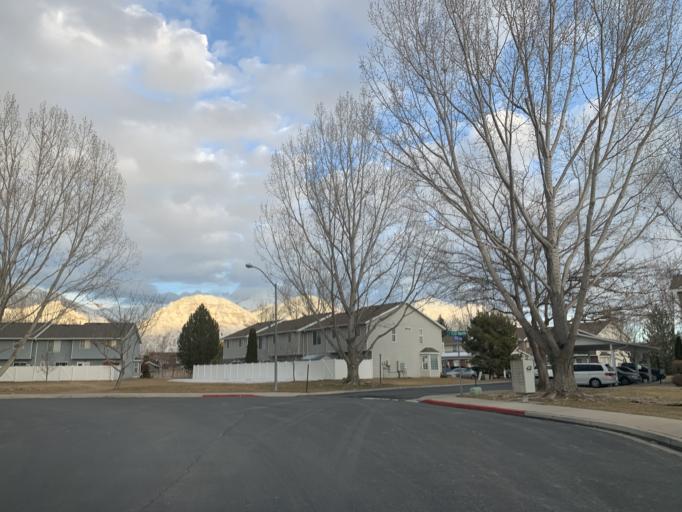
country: US
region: Utah
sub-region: Utah County
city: Orem
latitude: 40.2488
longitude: -111.7092
